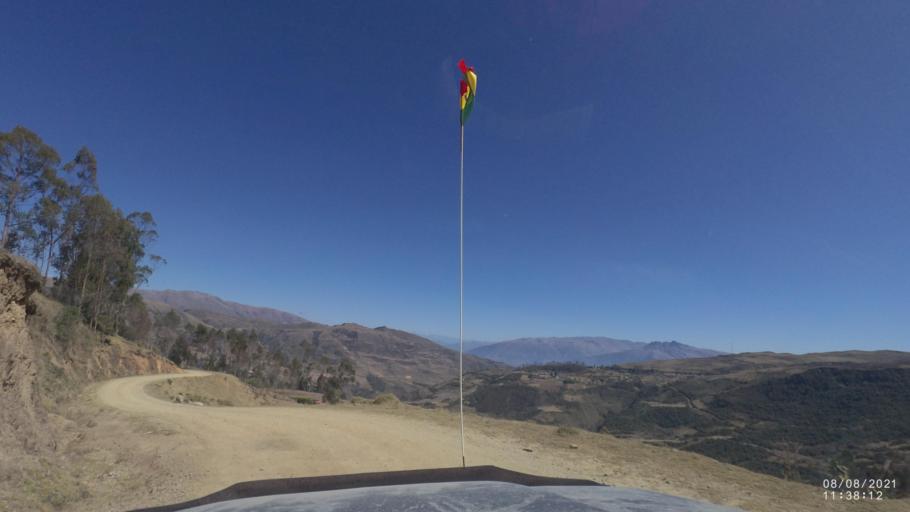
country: BO
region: Cochabamba
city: Colchani
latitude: -16.7883
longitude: -66.6497
